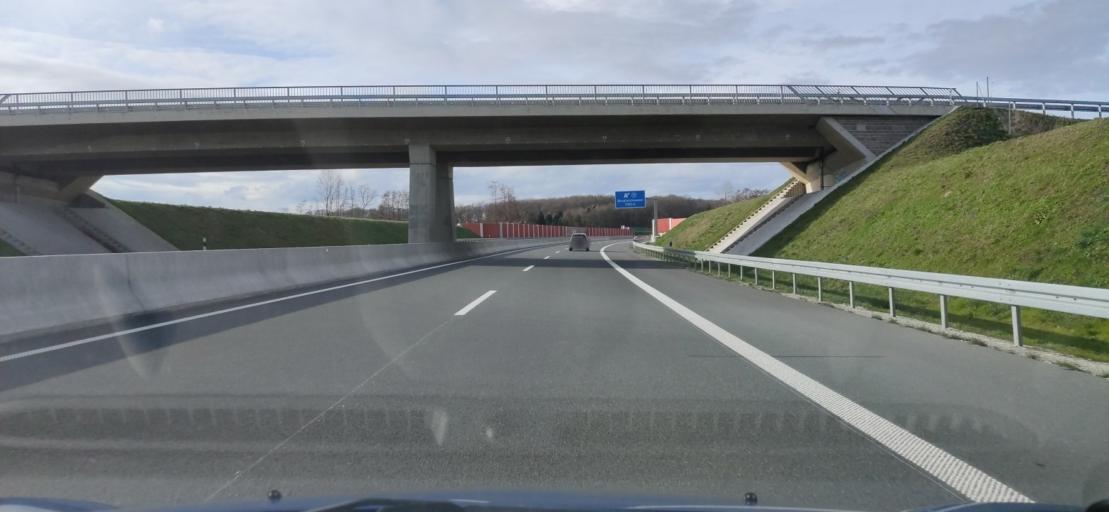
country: DE
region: North Rhine-Westphalia
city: Borgholzhausen
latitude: 52.0685
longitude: 8.2630
